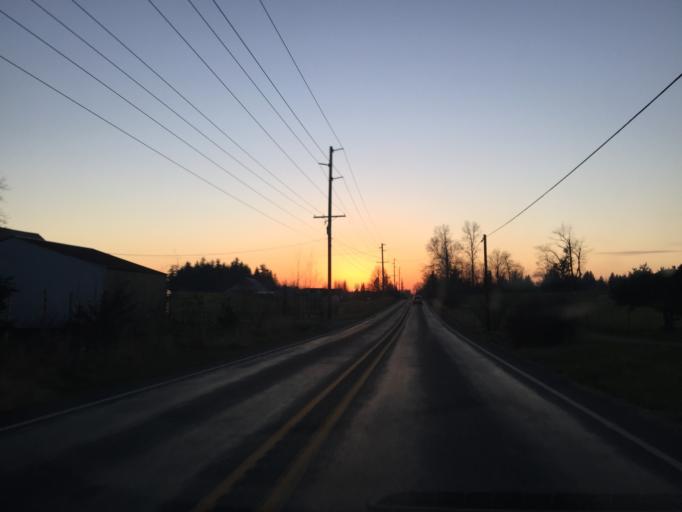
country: US
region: Washington
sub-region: Whatcom County
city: Nooksack
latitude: 48.9638
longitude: -122.3393
